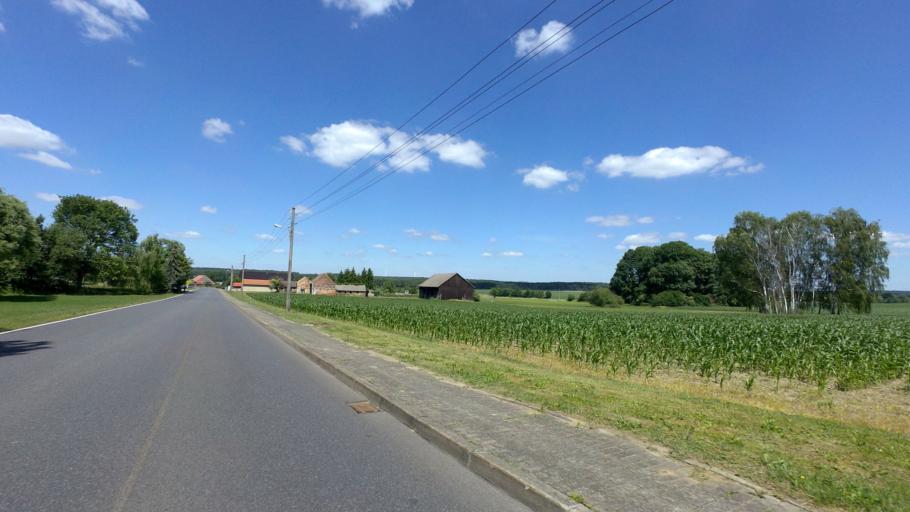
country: DE
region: Brandenburg
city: Kasel-Golzig
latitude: 51.8980
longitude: 13.6804
